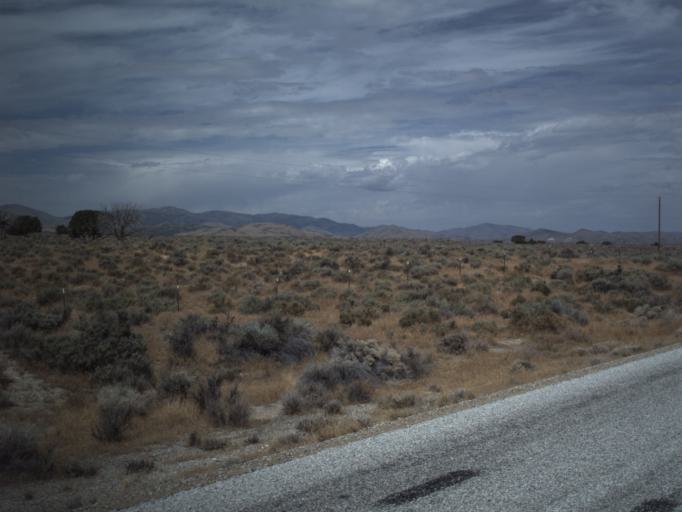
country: US
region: Utah
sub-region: Tooele County
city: Wendover
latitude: 41.5223
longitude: -113.5968
